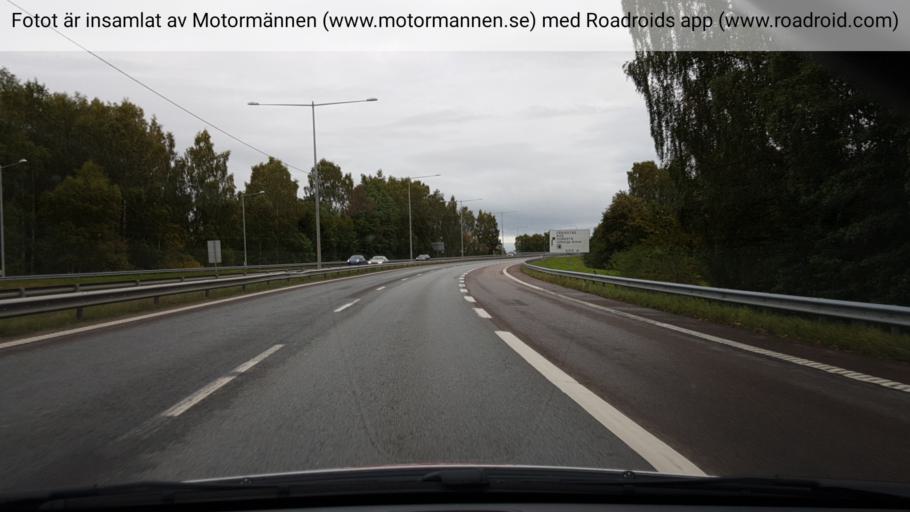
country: SE
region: Vaermland
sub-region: Karlstads Kommun
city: Karlstad
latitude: 59.3967
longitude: 13.4993
